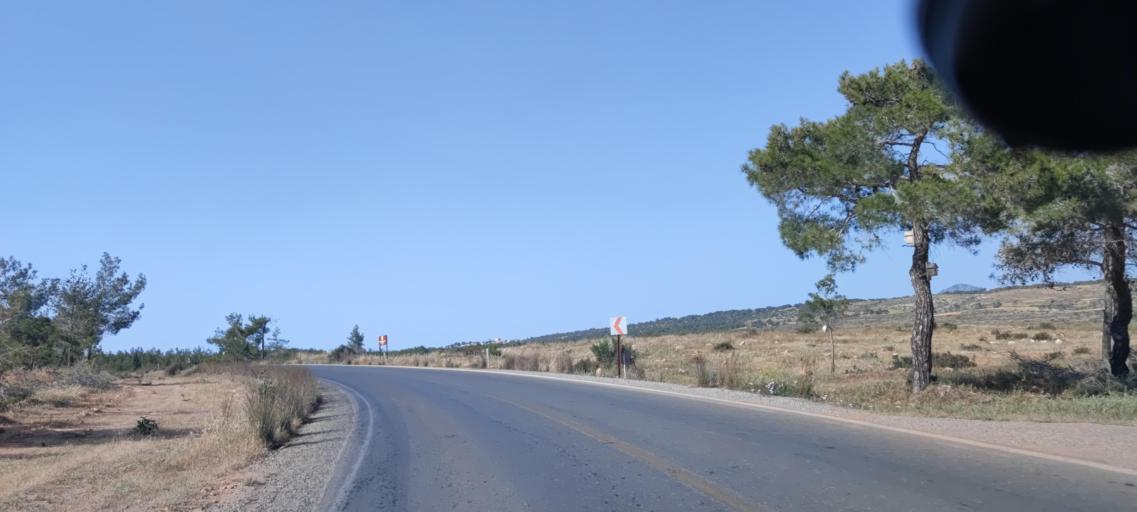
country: CY
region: Lefkosia
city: Morfou
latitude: 35.2811
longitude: 33.0409
